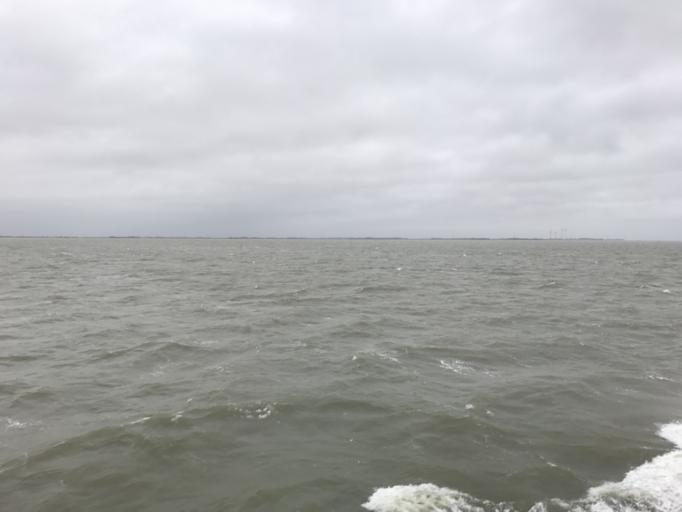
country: NL
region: Groningen
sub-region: Gemeente Delfzijl
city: Delfzijl
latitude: 53.4031
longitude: 6.9476
